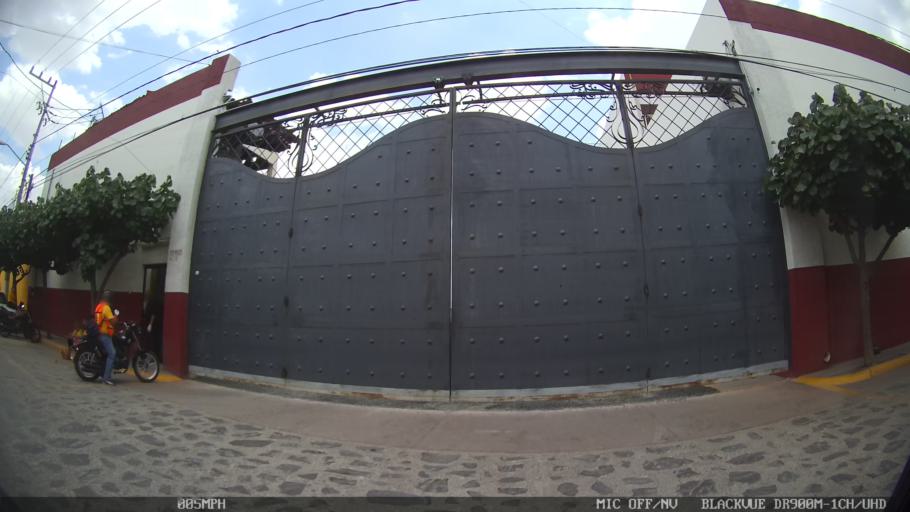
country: MX
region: Jalisco
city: Tonala
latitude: 20.6531
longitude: -103.2325
